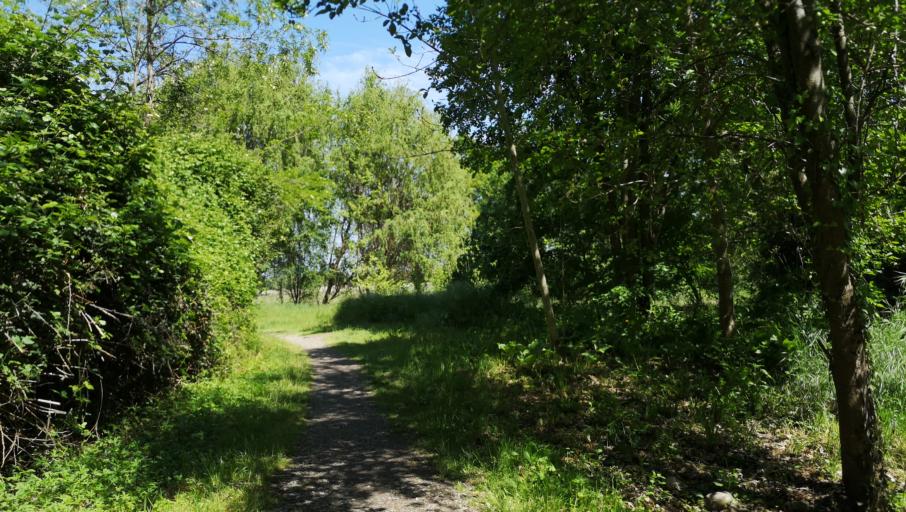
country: FR
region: Midi-Pyrenees
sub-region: Departement de la Haute-Garonne
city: Beauzelle
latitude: 43.6545
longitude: 1.3896
